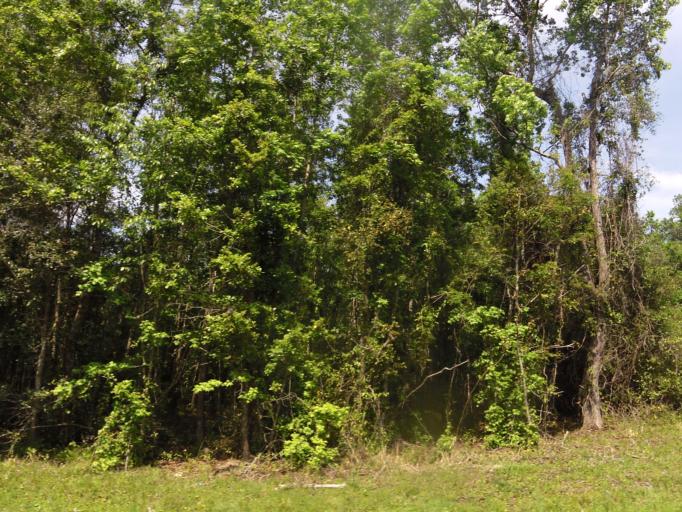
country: US
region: Georgia
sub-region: Camden County
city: Kingsland
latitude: 30.8003
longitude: -81.7237
